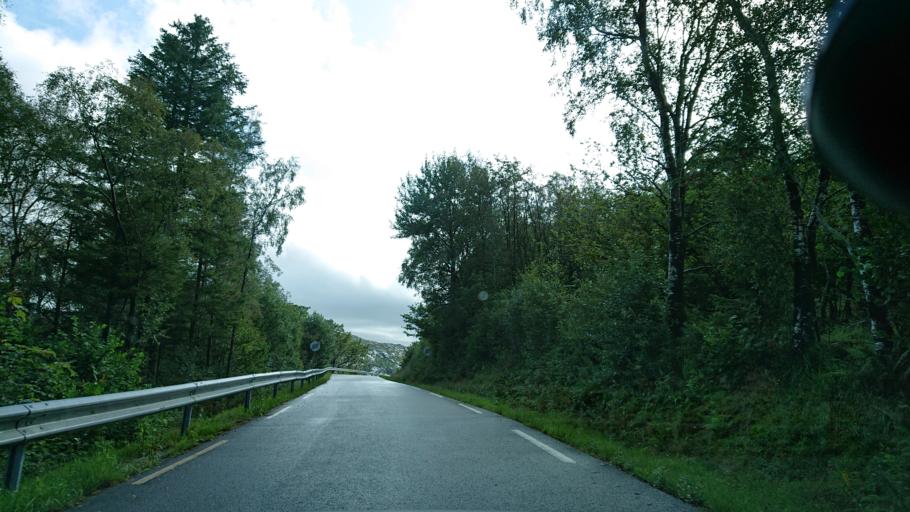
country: NO
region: Rogaland
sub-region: Gjesdal
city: Algard
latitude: 58.6927
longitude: 5.8808
